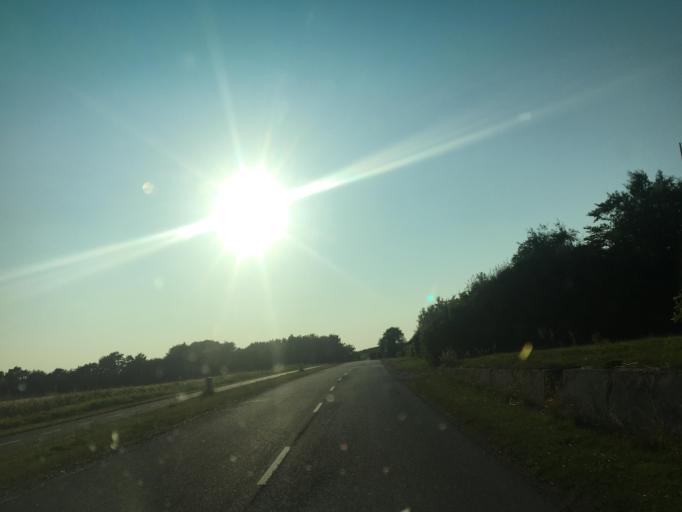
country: DK
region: North Denmark
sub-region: Thisted Kommune
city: Hurup
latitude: 56.8154
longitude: 8.3892
